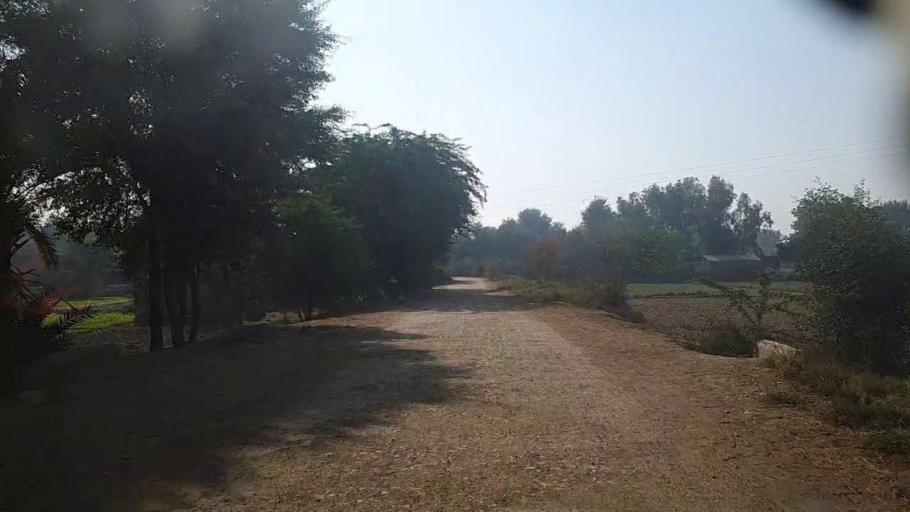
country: PK
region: Sindh
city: Kandiari
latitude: 27.0256
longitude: 68.5058
